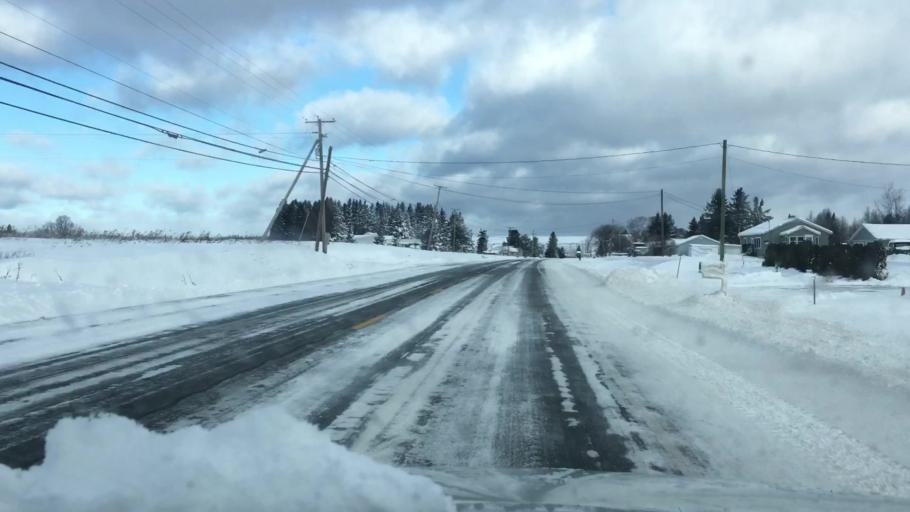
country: US
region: Maine
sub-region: Aroostook County
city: Caribou
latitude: 46.8910
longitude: -68.0151
